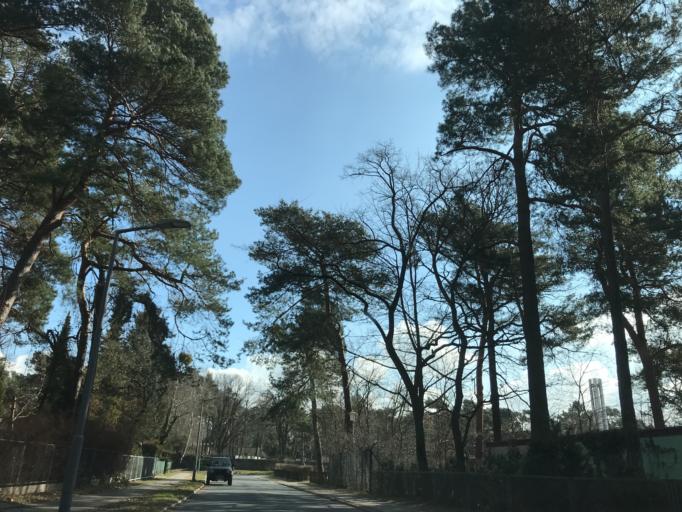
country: DE
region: Berlin
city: Kladow
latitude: 52.4505
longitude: 13.1203
